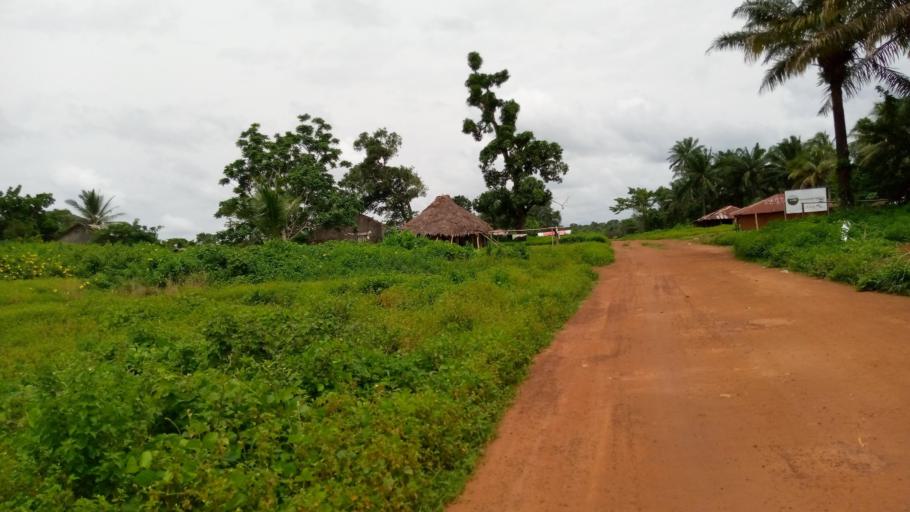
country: SL
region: Southern Province
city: Moyamba
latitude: 8.1750
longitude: -12.5005
